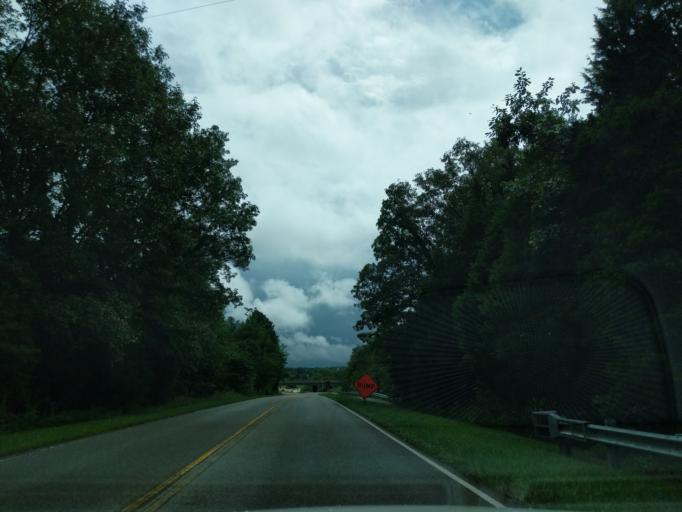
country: US
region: Kentucky
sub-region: Barren County
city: Cave City
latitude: 37.1013
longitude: -86.0566
